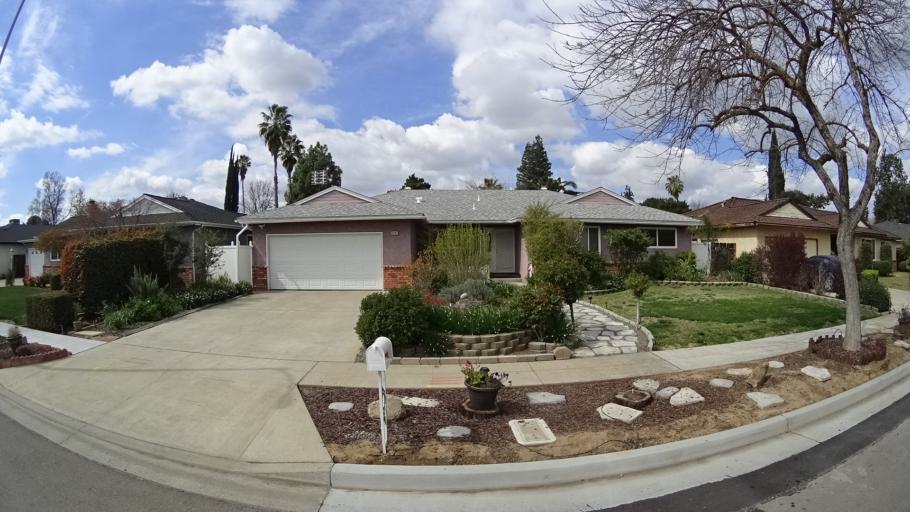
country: US
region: California
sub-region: Fresno County
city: Fresno
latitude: 36.8184
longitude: -119.8507
